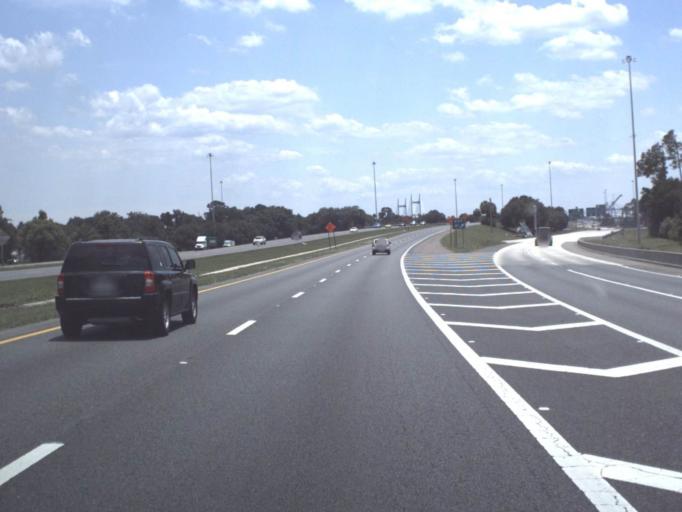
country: US
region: Florida
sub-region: Duval County
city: Jacksonville
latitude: 30.4172
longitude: -81.5656
